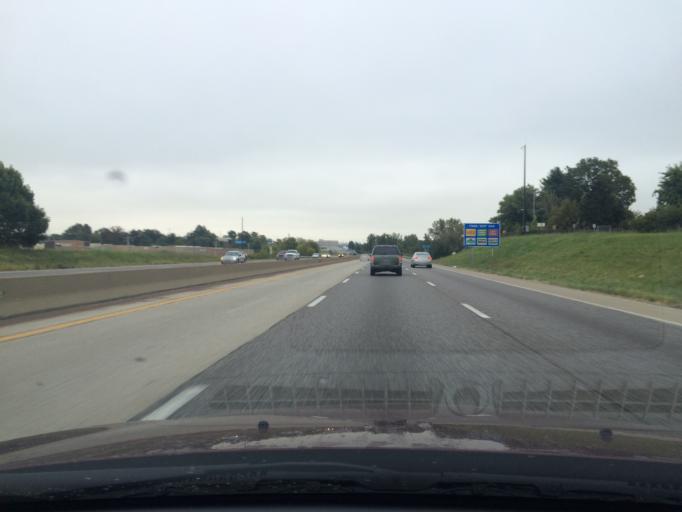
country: US
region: Missouri
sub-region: Saint Louis County
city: Bridgeton
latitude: 38.7442
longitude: -90.4231
